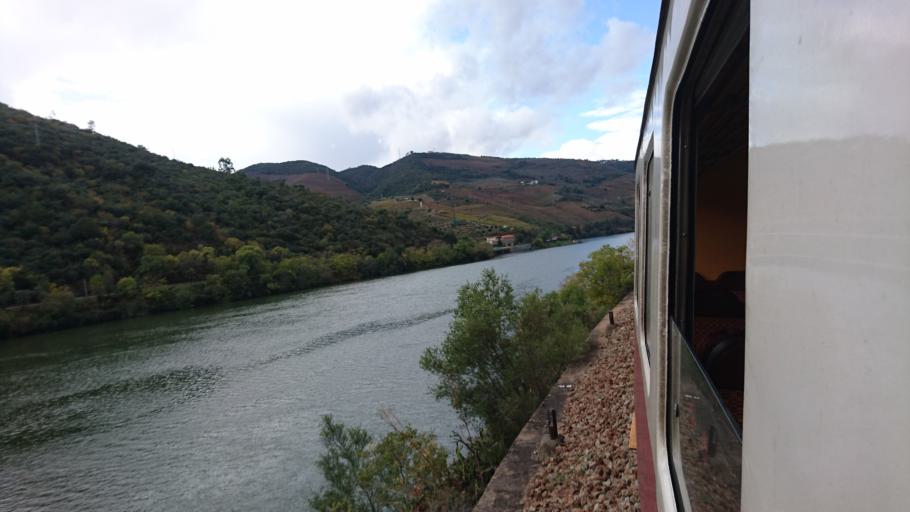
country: PT
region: Viseu
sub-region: Tabuaco
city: Tabuaco
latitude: 41.1612
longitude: -7.5766
